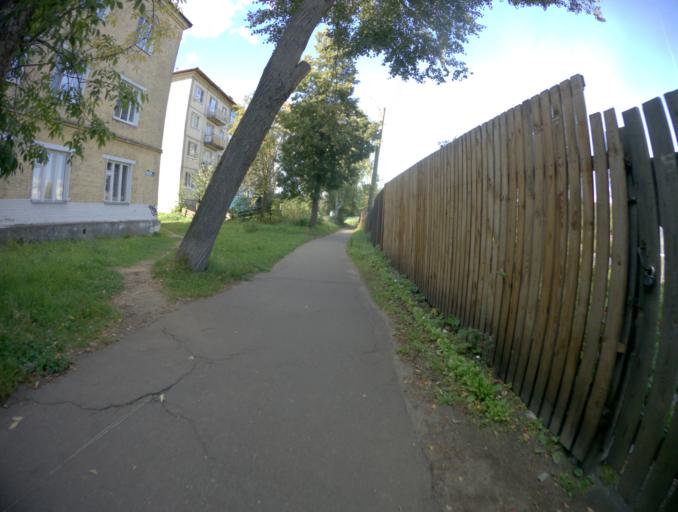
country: RU
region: Vladimir
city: Petushki
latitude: 55.9220
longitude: 39.4652
